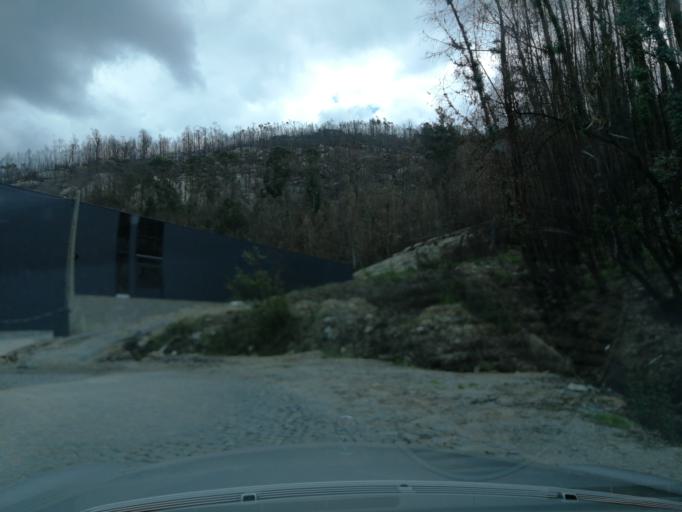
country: PT
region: Braga
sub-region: Braga
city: Braga
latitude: 41.5231
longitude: -8.4004
